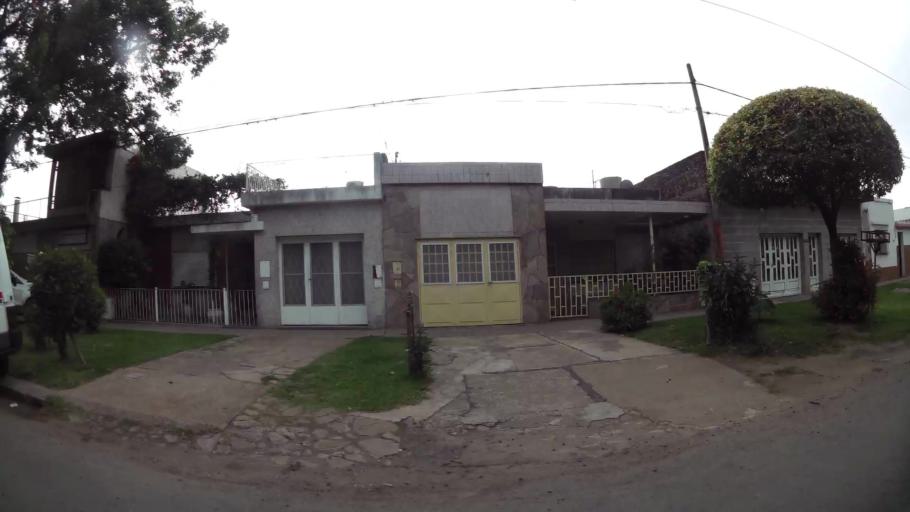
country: AR
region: Santa Fe
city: Gobernador Galvez
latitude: -33.0025
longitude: -60.6778
